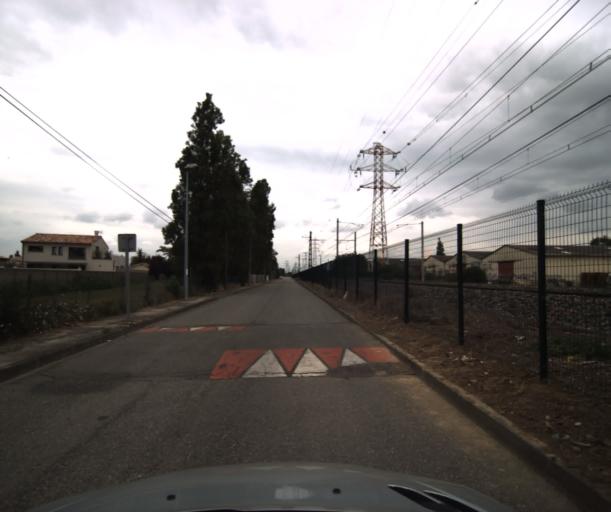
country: FR
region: Midi-Pyrenees
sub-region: Departement de la Haute-Garonne
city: Portet-sur-Garonne
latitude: 43.5391
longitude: 1.3983
